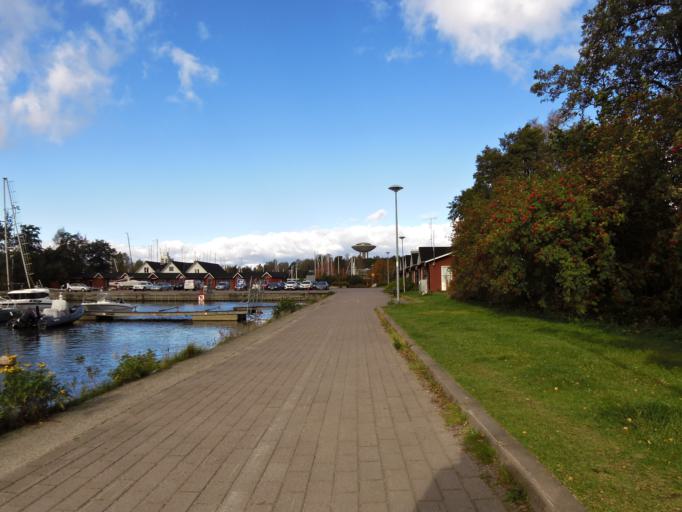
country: FI
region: Uusimaa
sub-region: Helsinki
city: Koukkuniemi
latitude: 60.1551
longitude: 24.7732
